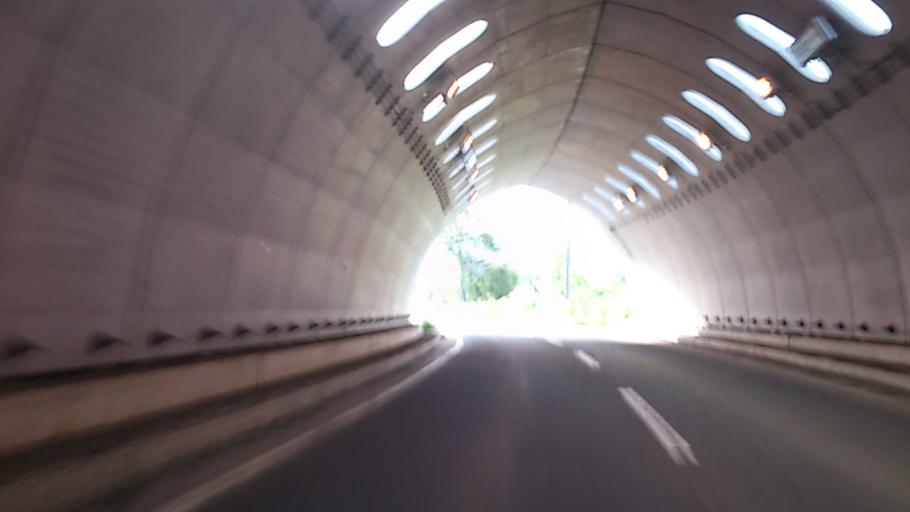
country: JP
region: Aomori
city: Aomori Shi
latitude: 40.6420
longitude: 140.8088
